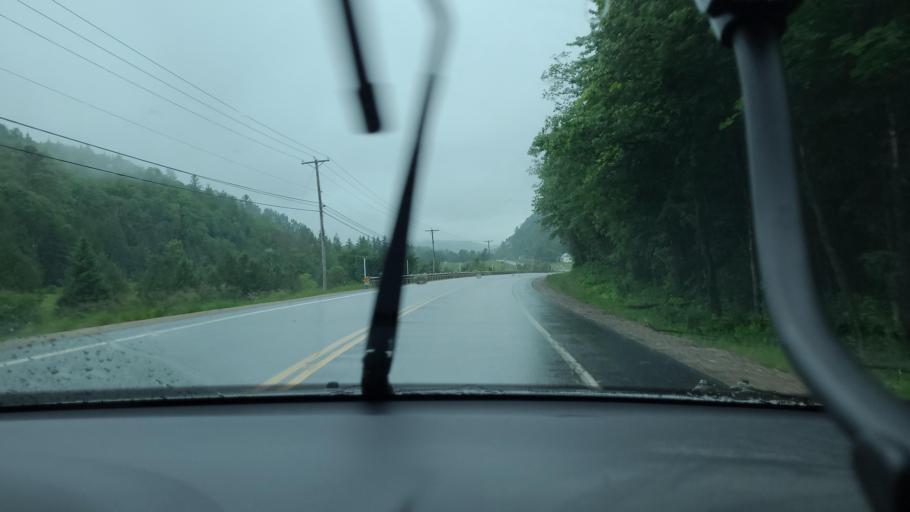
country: CA
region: Quebec
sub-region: Outaouais
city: Saint-Andre-Avellin
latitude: 45.8547
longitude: -75.0485
